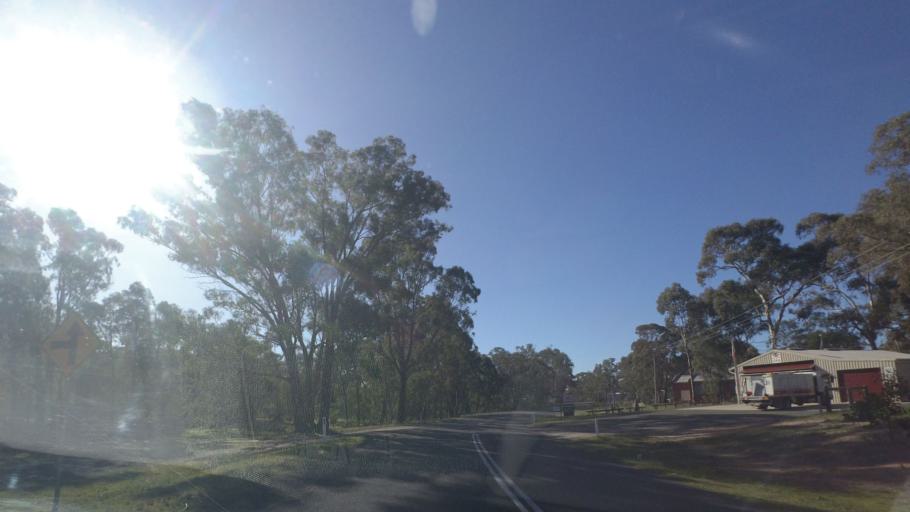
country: AU
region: Victoria
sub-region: Greater Bendigo
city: Kennington
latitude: -36.8720
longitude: 144.3149
